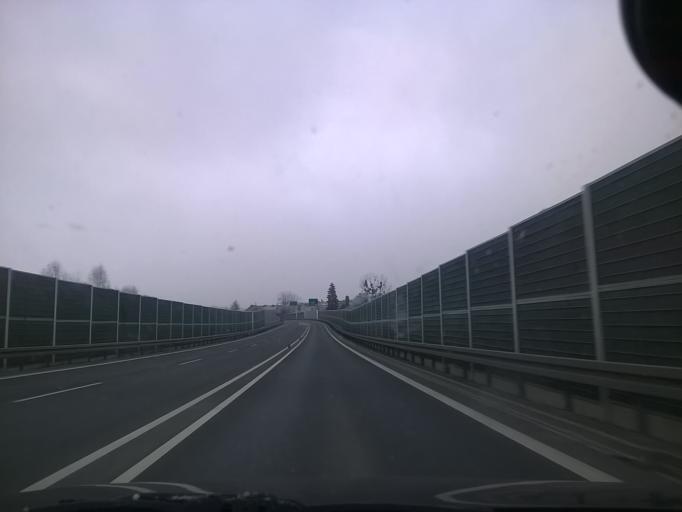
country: PL
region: Warmian-Masurian Voivodeship
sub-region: Powiat mragowski
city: Mragowo
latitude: 53.8787
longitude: 21.2967
